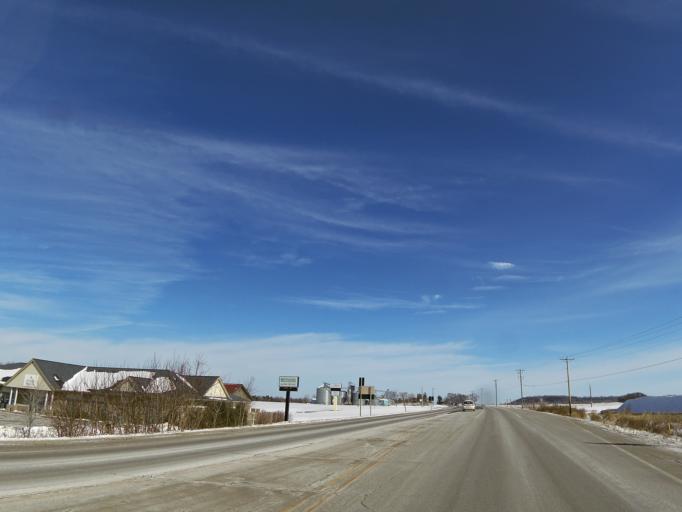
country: US
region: Wisconsin
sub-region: Pierce County
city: Prescott
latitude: 44.7630
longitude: -92.7903
